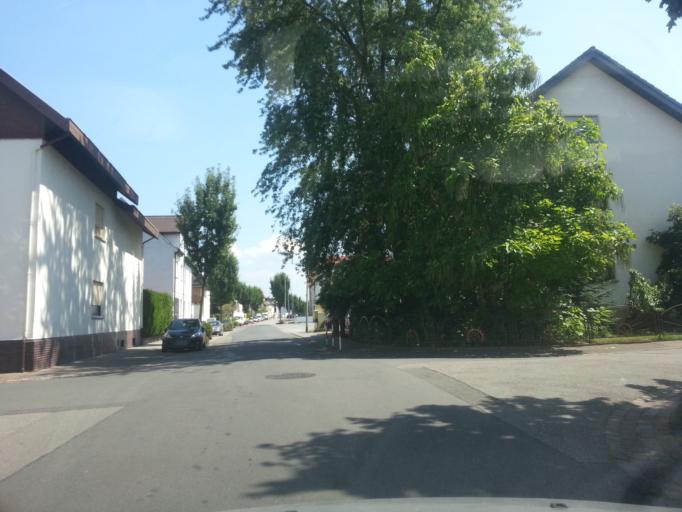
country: DE
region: Hesse
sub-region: Regierungsbezirk Darmstadt
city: Burstadt
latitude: 49.6377
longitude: 8.4543
